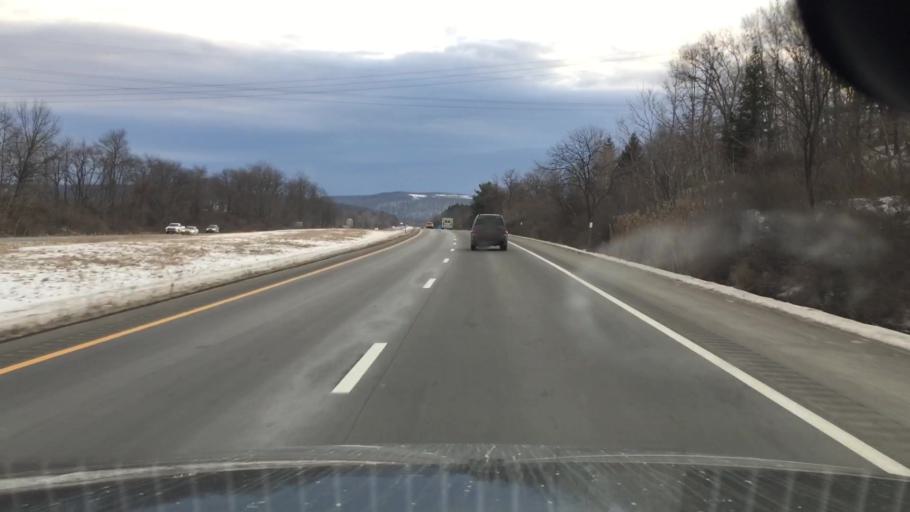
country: US
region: New York
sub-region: Tioga County
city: Waverly
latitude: 42.0003
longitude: -76.5127
